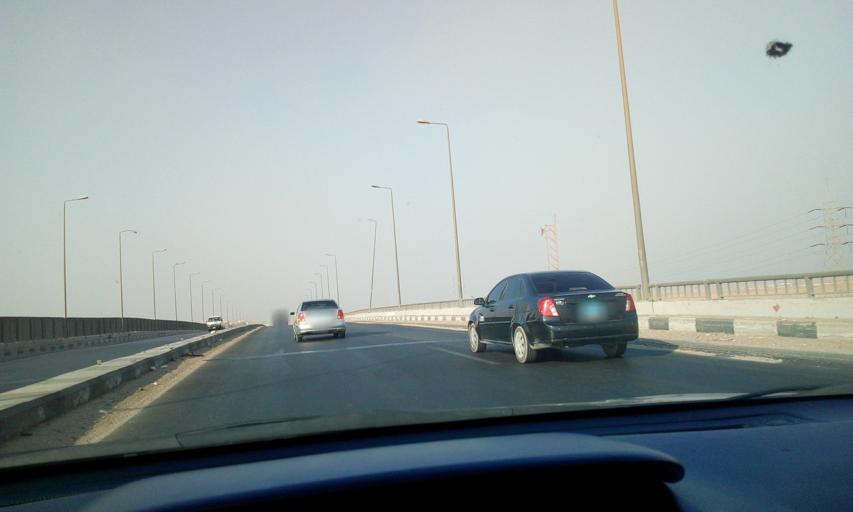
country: EG
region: Al Jizah
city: Madinat Sittah Uktubar
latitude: 29.8746
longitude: 31.0753
